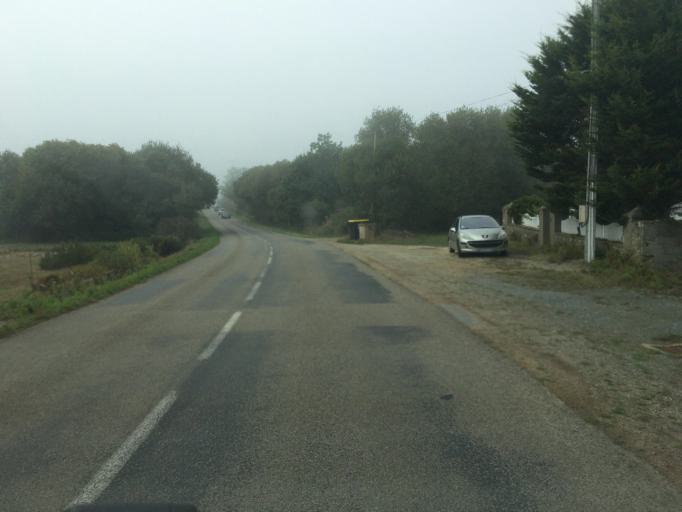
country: FR
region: Brittany
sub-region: Departement du Finistere
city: Plogoff
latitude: 48.0614
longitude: -4.6539
